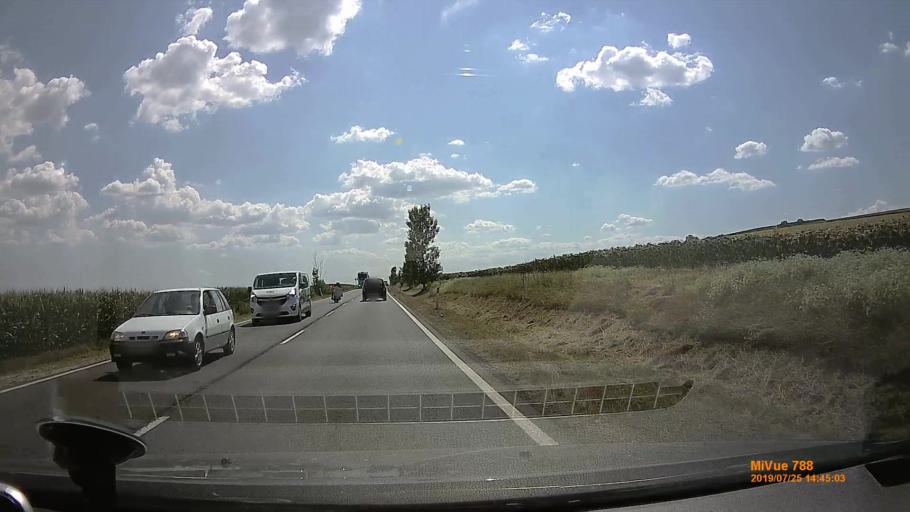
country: HU
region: Borsod-Abauj-Zemplen
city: Halmaj
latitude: 48.2634
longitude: 20.9946
